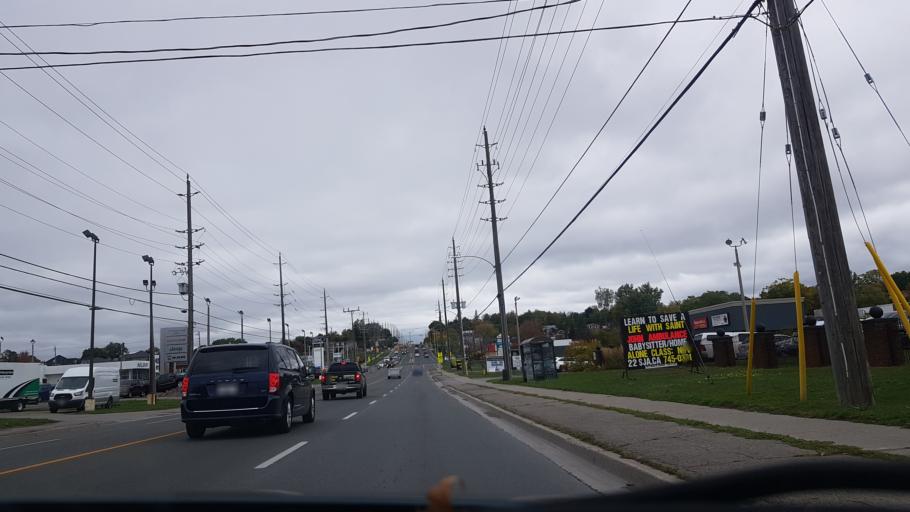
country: CA
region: Ontario
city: Peterborough
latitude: 44.2780
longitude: -78.3621
